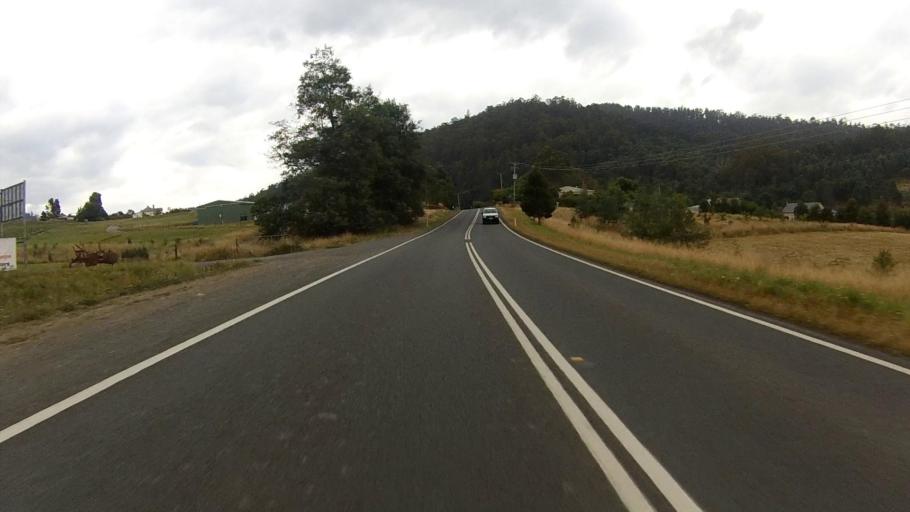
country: AU
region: Tasmania
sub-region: Huon Valley
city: Cygnet
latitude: -43.1434
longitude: 147.0641
